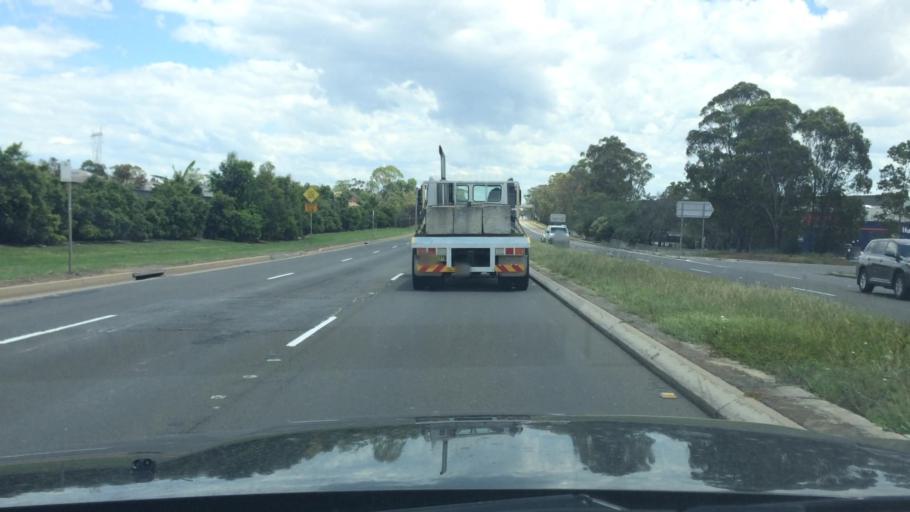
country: AU
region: New South Wales
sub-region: Campbelltown Municipality
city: Glenfield
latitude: -33.9606
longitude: 150.8839
